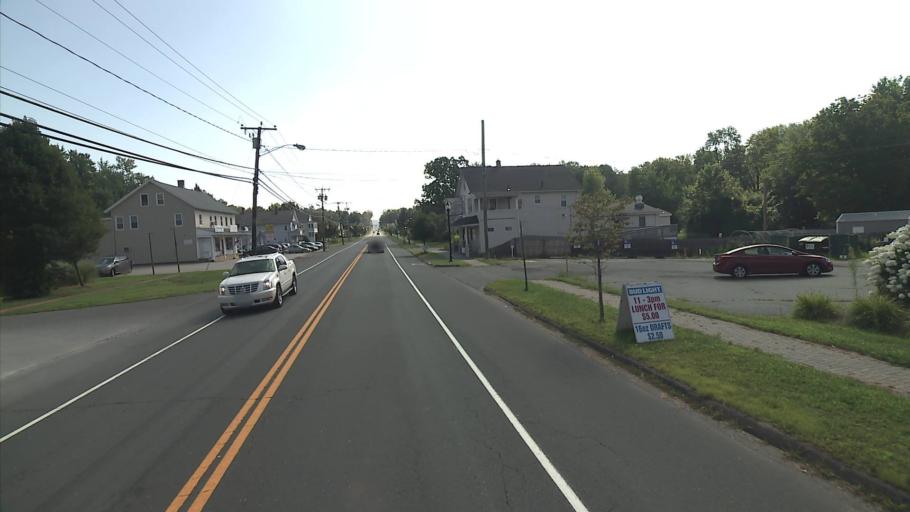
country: US
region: Connecticut
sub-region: Tolland County
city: Somers
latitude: 41.9851
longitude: -72.4902
